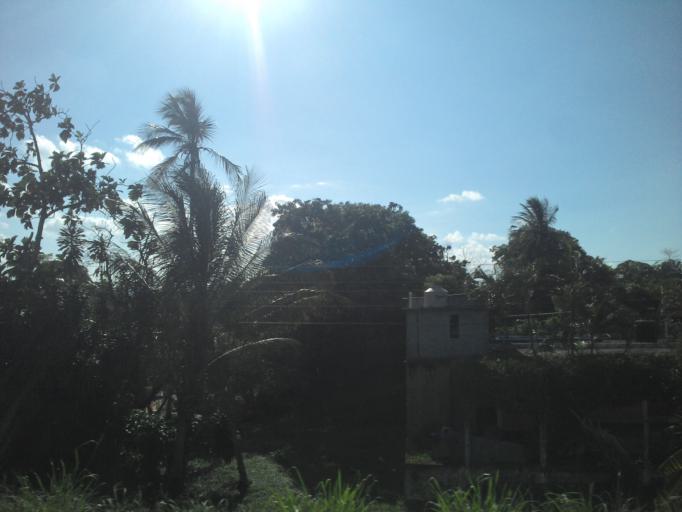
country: MX
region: Chiapas
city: Palenque
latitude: 17.5468
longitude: -91.9838
